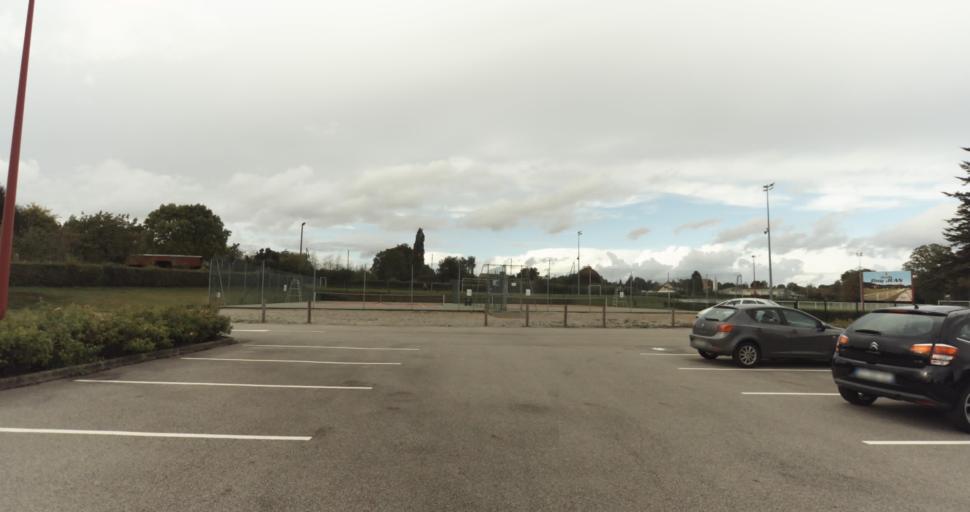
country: FR
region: Lower Normandy
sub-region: Departement de l'Orne
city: Gace
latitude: 48.7005
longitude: 0.2800
